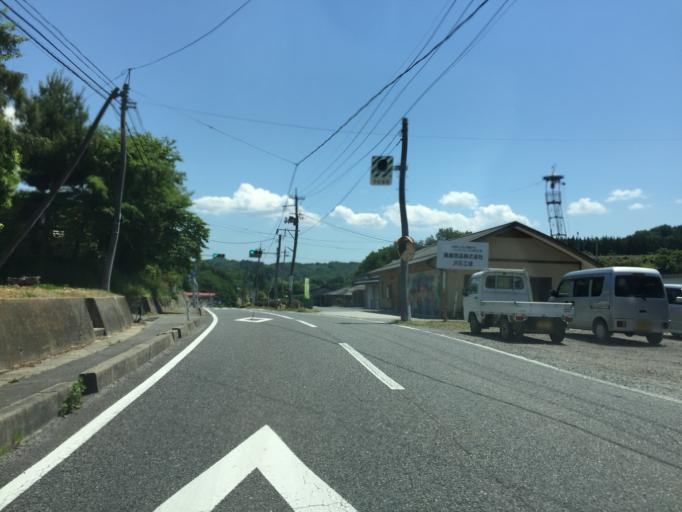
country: JP
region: Fukushima
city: Funehikimachi-funehiki
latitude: 37.4881
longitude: 140.5359
